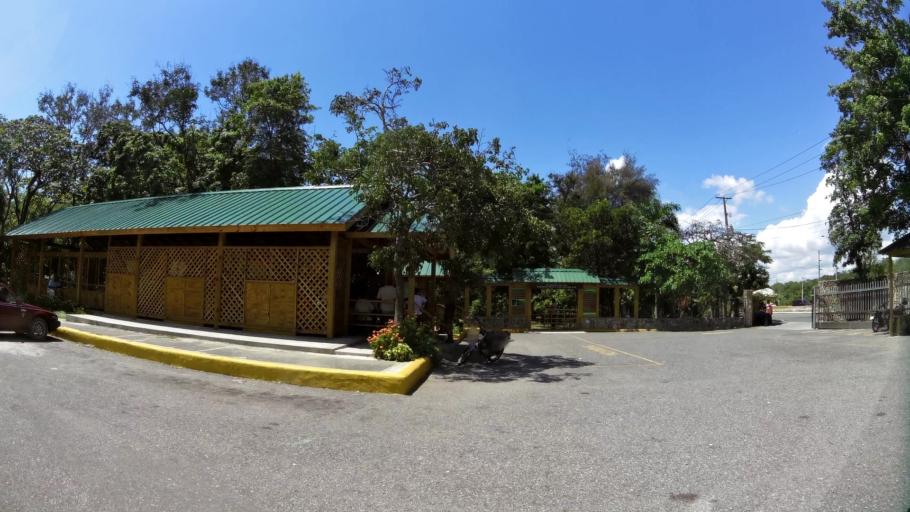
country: DO
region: Santo Domingo
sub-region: Santo Domingo
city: Santo Domingo Este
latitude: 18.4812
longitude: -69.8435
